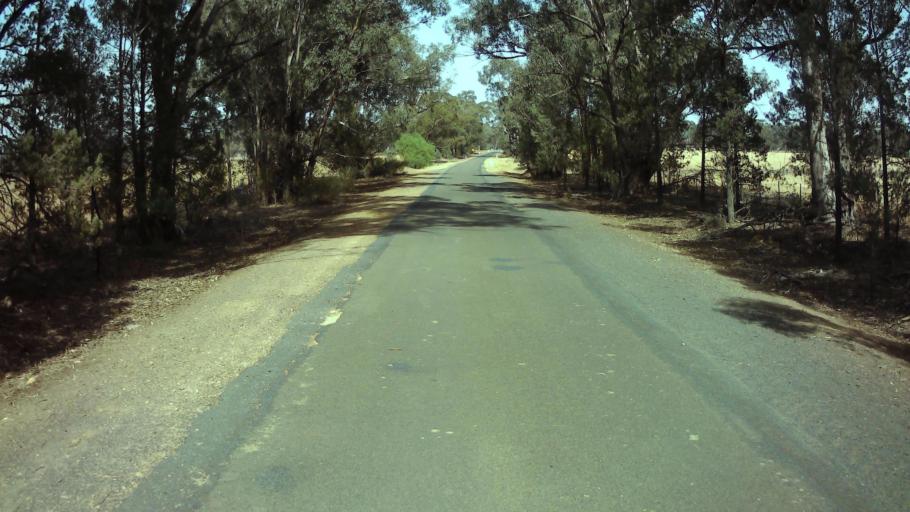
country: AU
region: New South Wales
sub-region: Weddin
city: Grenfell
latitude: -33.8706
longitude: 148.0933
